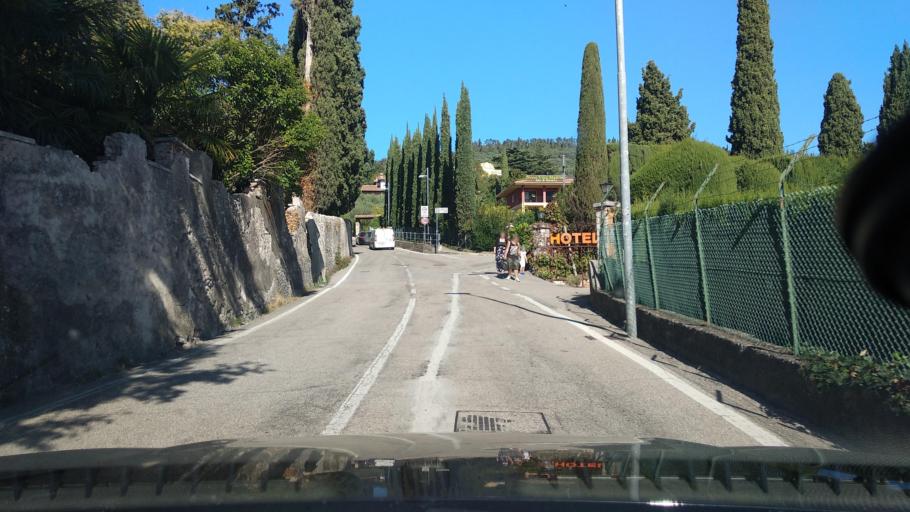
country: IT
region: Veneto
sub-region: Provincia di Verona
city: Garda
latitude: 45.5780
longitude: 10.7054
